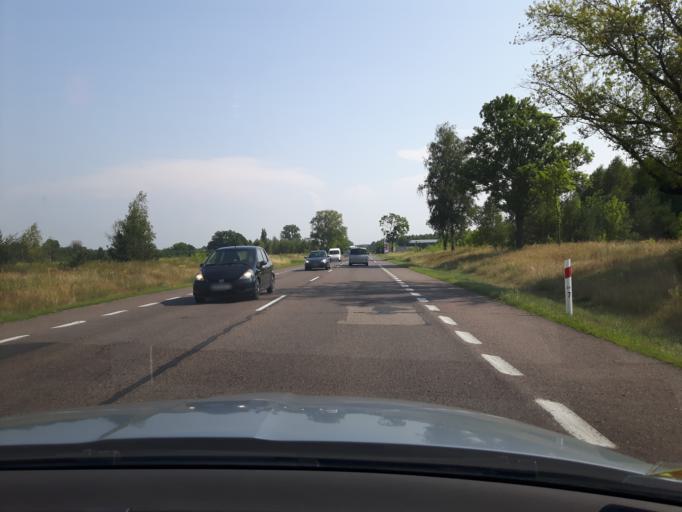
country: PL
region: Masovian Voivodeship
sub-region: Powiat ciechanowski
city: Glinojeck
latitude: 52.7812
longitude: 20.2865
